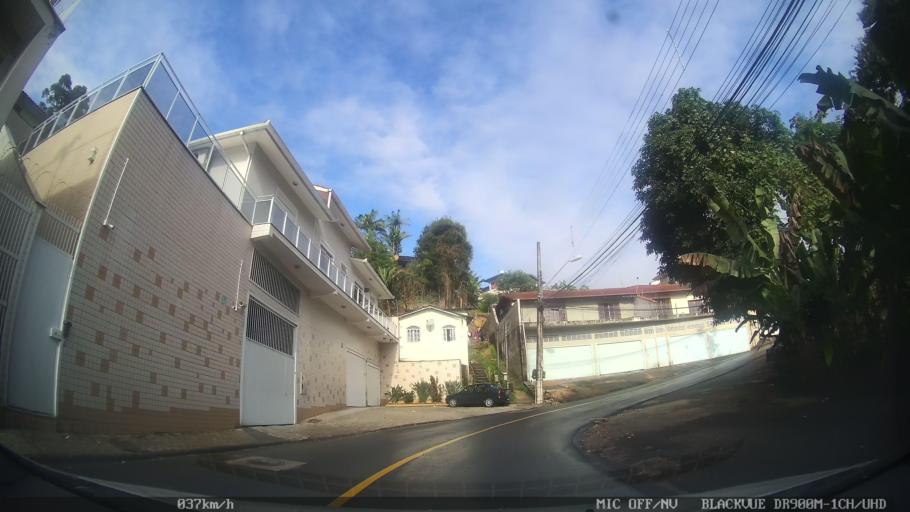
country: BR
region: Santa Catarina
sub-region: Sao Jose
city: Campinas
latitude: -27.6147
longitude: -48.6340
